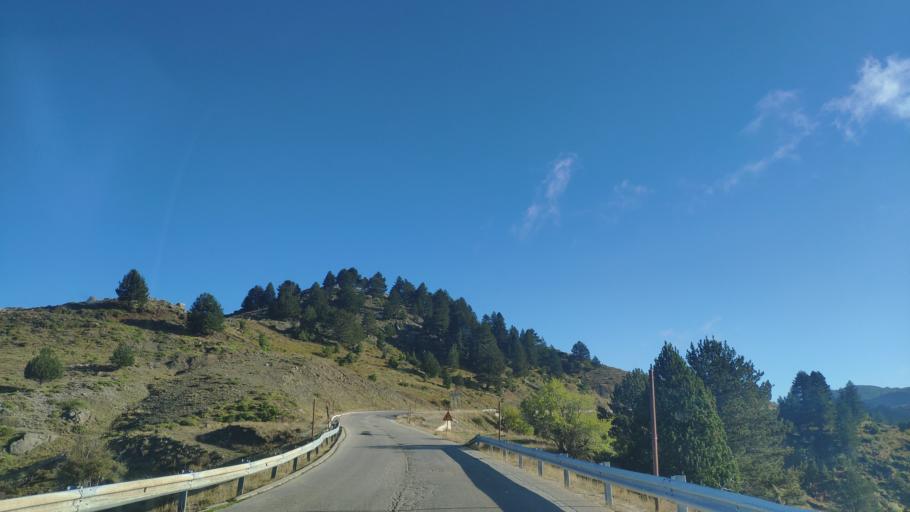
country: GR
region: Epirus
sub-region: Nomos Ioanninon
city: Metsovo
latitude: 39.7957
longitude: 21.1683
